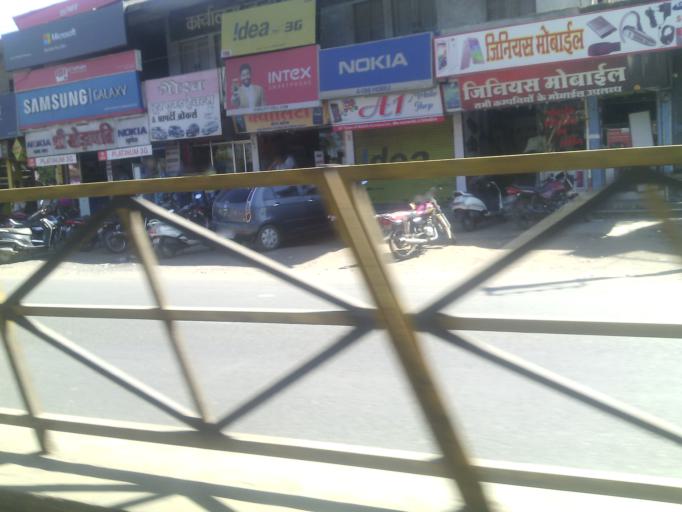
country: IN
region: Madhya Pradesh
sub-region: Dewas
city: Dewas
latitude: 22.9678
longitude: 76.0519
